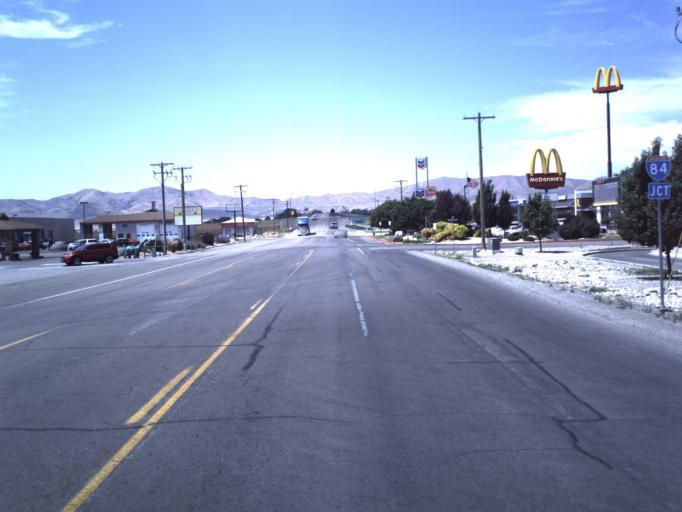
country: US
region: Utah
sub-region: Box Elder County
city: Tremonton
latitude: 41.7110
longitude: -112.1994
